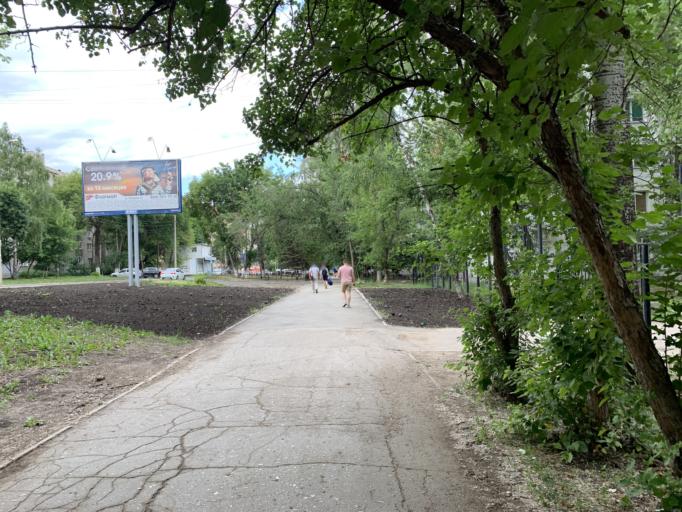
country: RU
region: Samara
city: Samara
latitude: 53.2125
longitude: 50.1699
